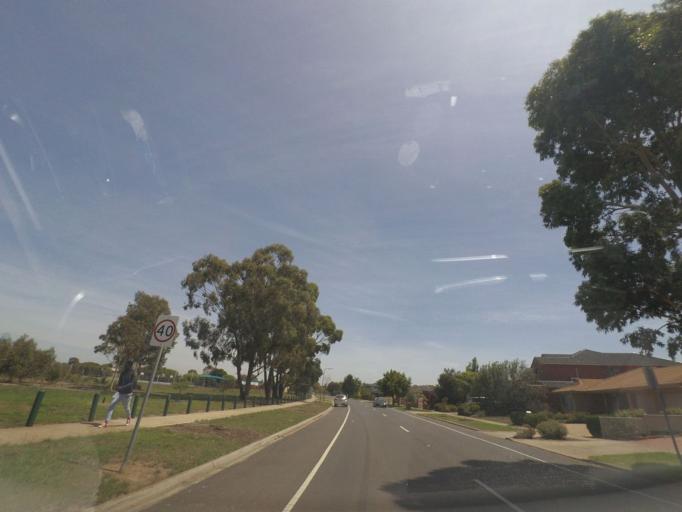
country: AU
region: Victoria
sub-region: Brimbank
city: Keilor Downs
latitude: -37.7158
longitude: 144.7944
